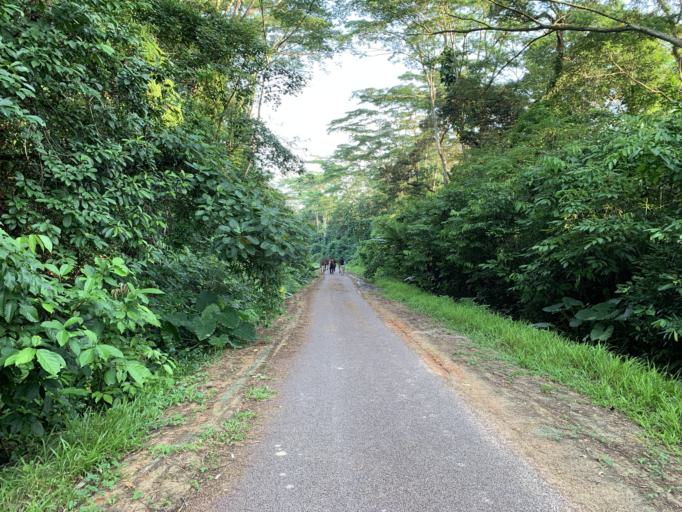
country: SG
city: Singapore
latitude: 1.3249
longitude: 103.7816
